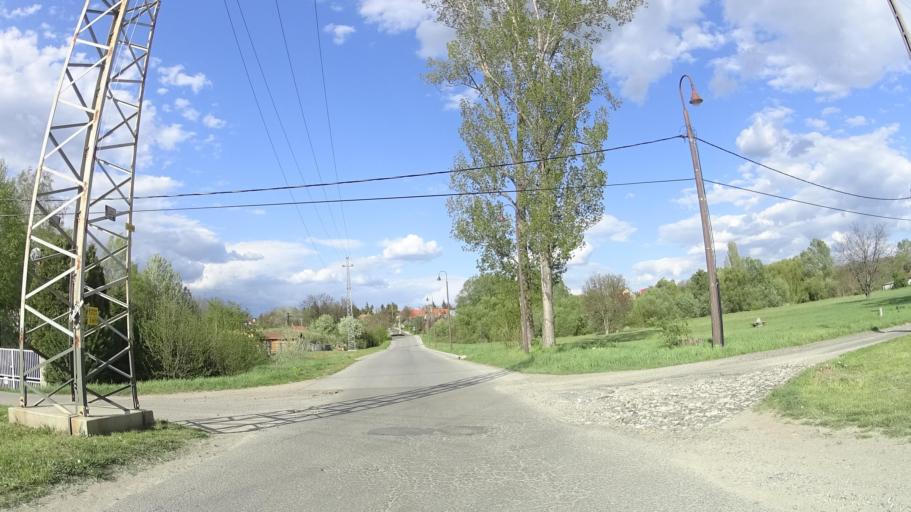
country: HU
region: Pest
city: Veresegyhaz
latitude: 47.6489
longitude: 19.2931
